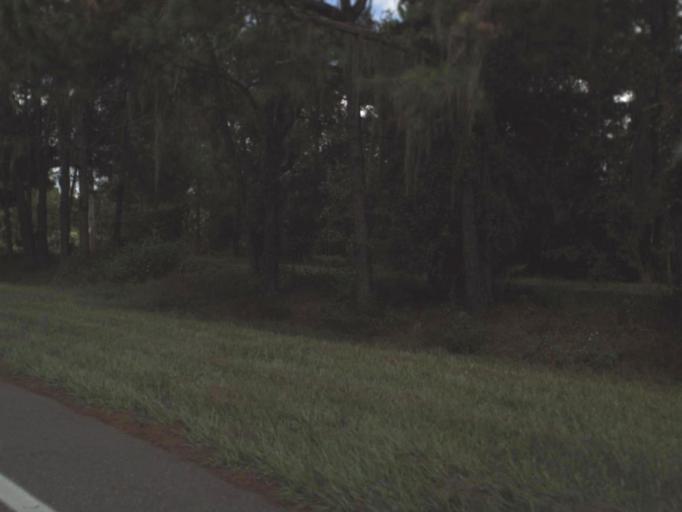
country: US
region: Florida
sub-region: Polk County
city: Mulberry
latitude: 27.7048
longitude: -82.0241
